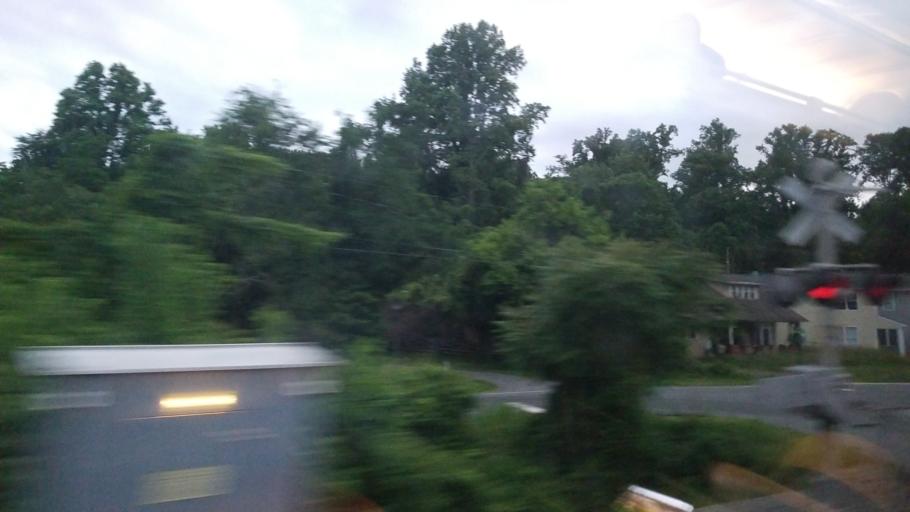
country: US
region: Virginia
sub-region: Orange County
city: Orange
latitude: 38.2423
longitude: -78.1195
